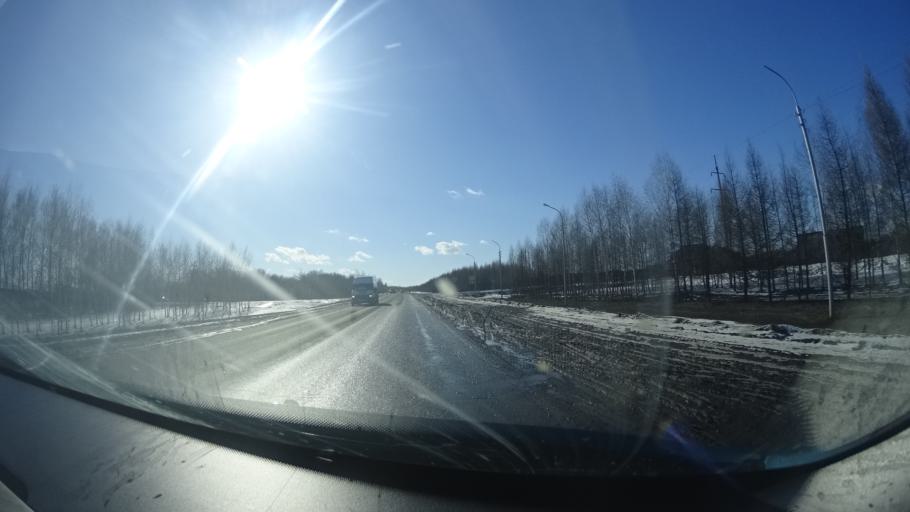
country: RU
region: Bashkortostan
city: Chishmy
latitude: 54.5805
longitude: 55.3715
